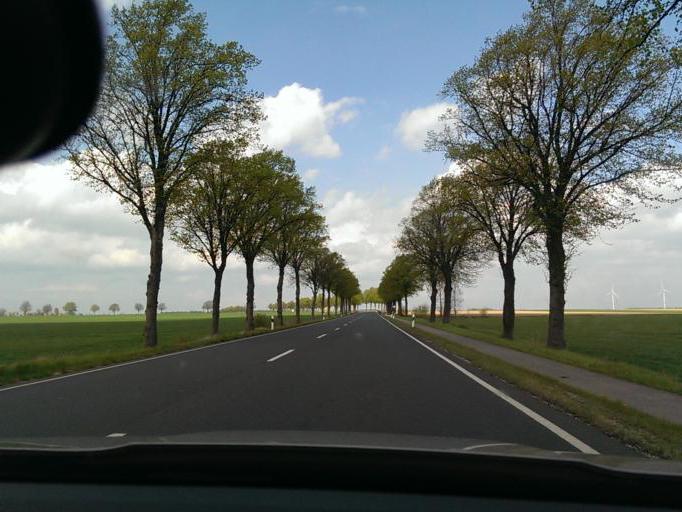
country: DE
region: Lower Saxony
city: Pattensen
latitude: 52.2269
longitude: 9.7530
